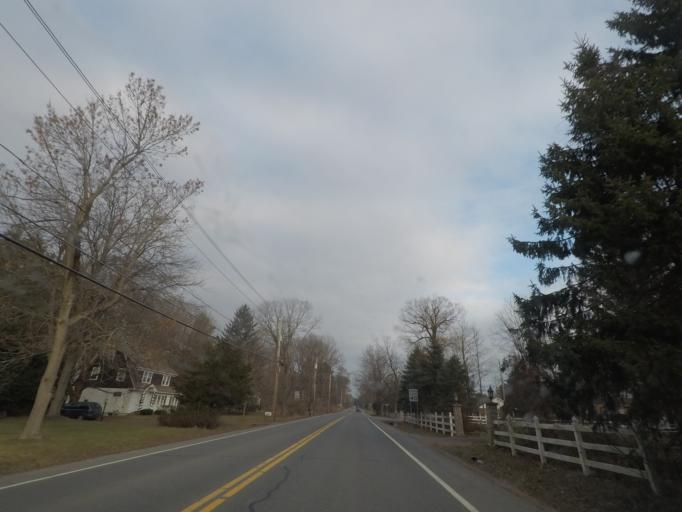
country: US
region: New York
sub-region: Rensselaer County
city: Wynantskill
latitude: 42.7268
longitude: -73.6538
